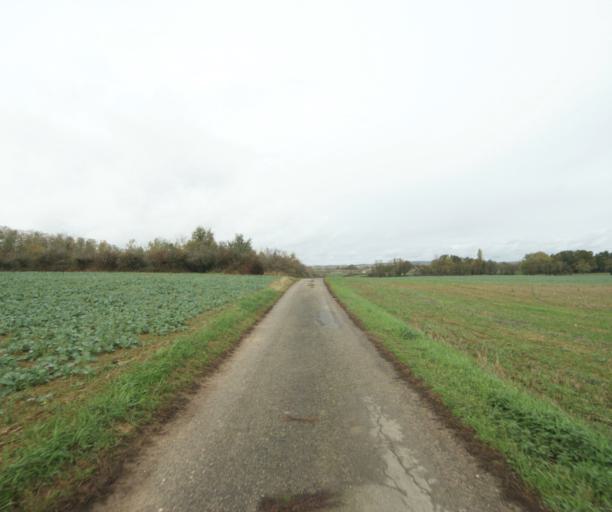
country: FR
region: Rhone-Alpes
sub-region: Departement de l'Ain
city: Pont-de-Vaux
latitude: 46.4567
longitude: 4.8808
